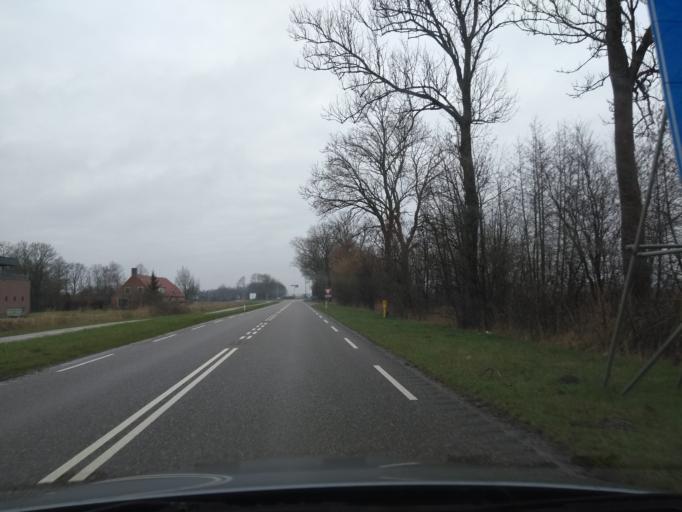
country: NL
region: Overijssel
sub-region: Gemeente Steenwijkerland
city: Vollenhove
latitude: 52.7091
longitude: 5.8790
